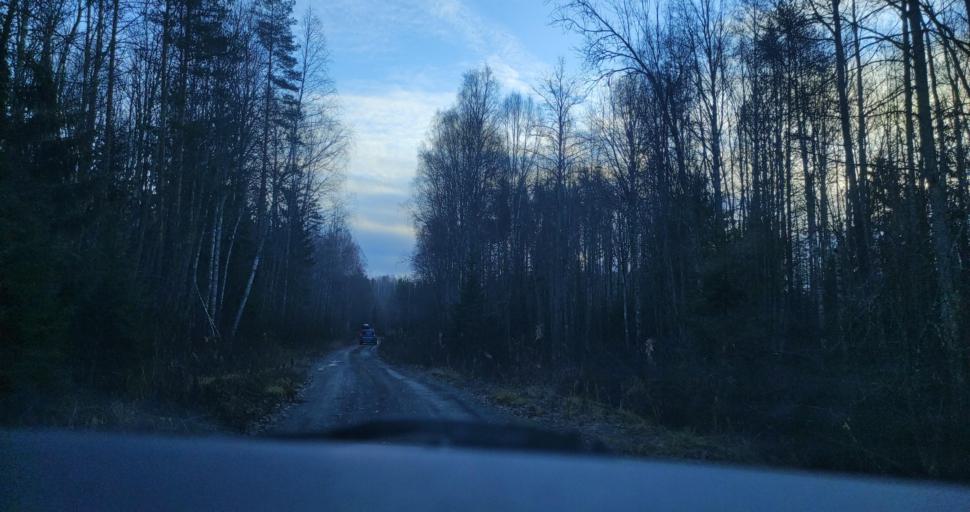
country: RU
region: Republic of Karelia
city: Pitkyaranta
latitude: 61.7330
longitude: 31.3753
